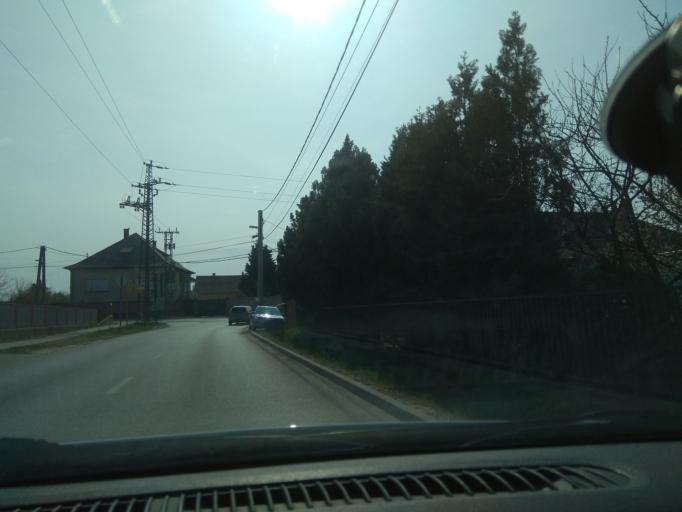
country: HU
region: Pest
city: Szigetszentmiklos
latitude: 47.3522
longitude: 19.0557
